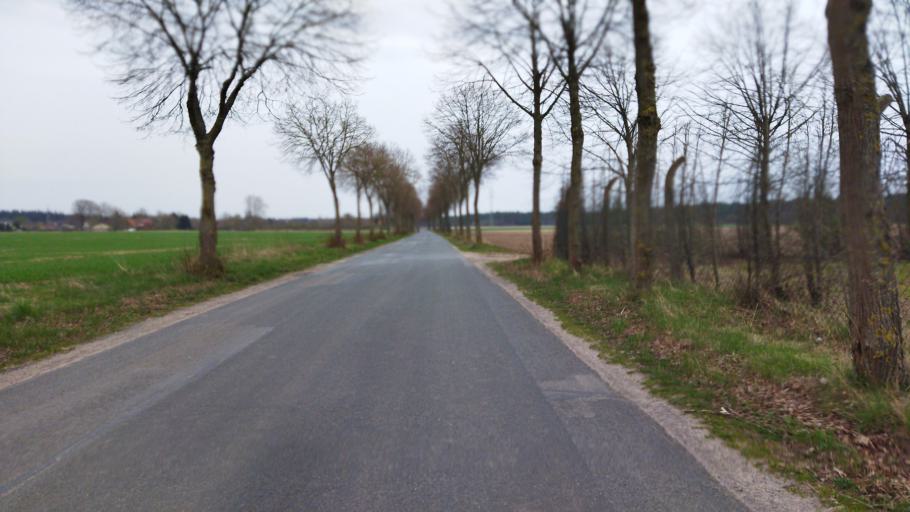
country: DE
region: Lower Saxony
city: Estorf
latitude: 52.5966
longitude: 9.1720
